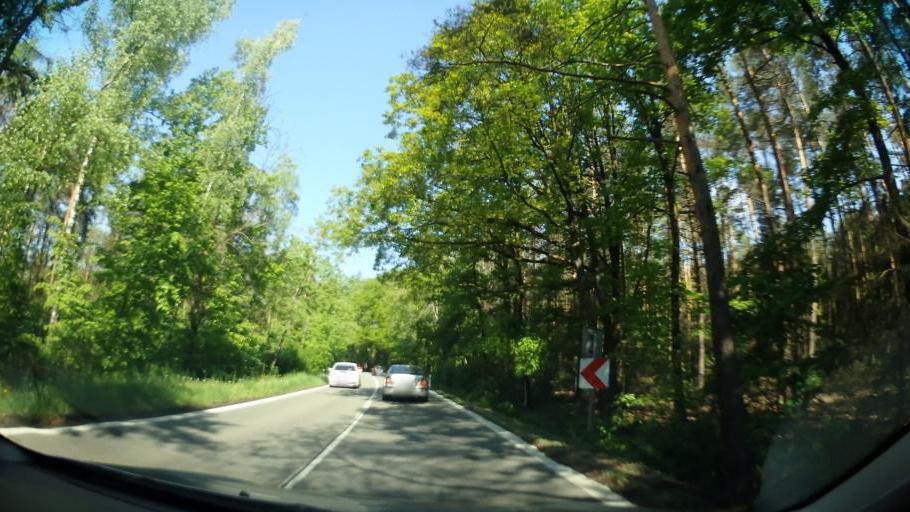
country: CZ
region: South Moravian
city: Zastavka
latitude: 49.1844
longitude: 16.3358
